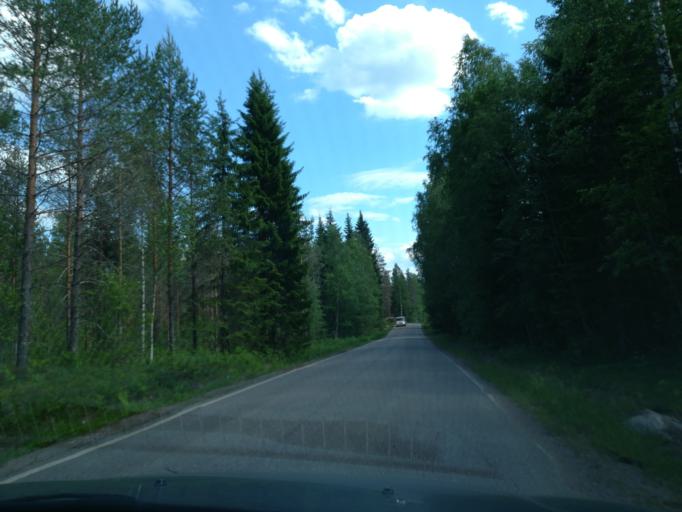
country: FI
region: South Karelia
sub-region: Imatra
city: Ruokolahti
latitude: 61.4724
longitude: 28.8096
